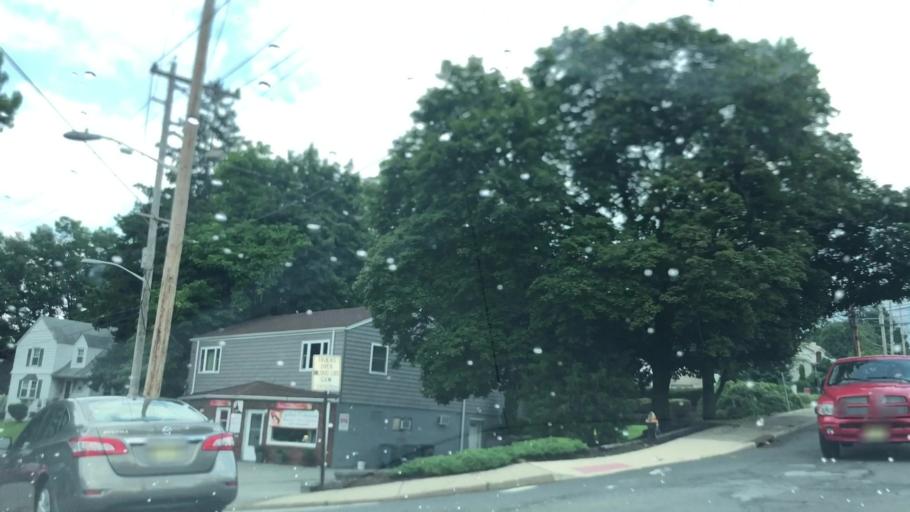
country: US
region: New Jersey
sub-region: Passaic County
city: Little Falls
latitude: 40.8769
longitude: -74.2156
